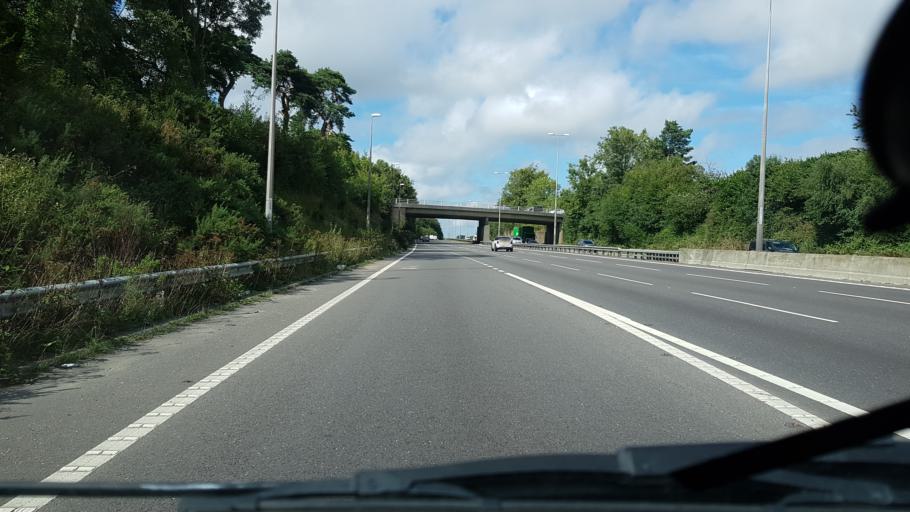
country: GB
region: England
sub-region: West Sussex
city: Broadfield
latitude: 51.0514
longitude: -0.2018
